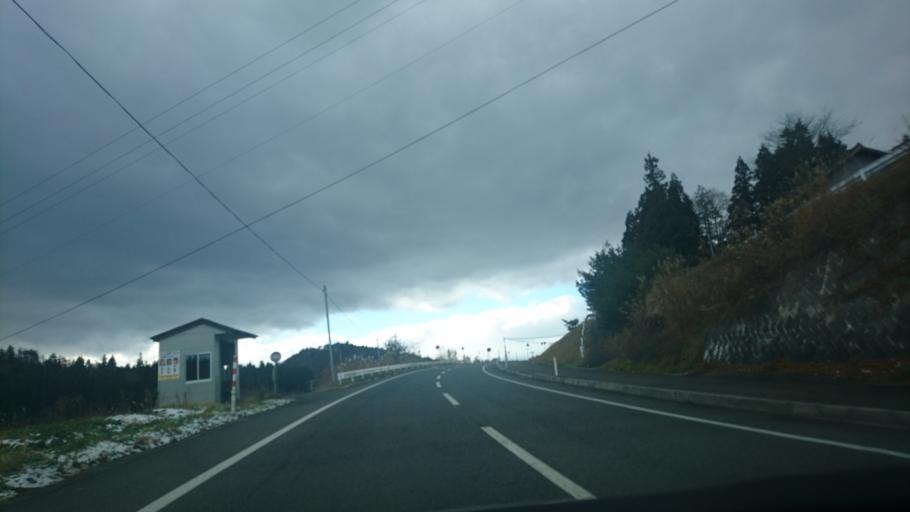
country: JP
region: Iwate
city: Mizusawa
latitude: 39.1766
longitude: 141.2775
